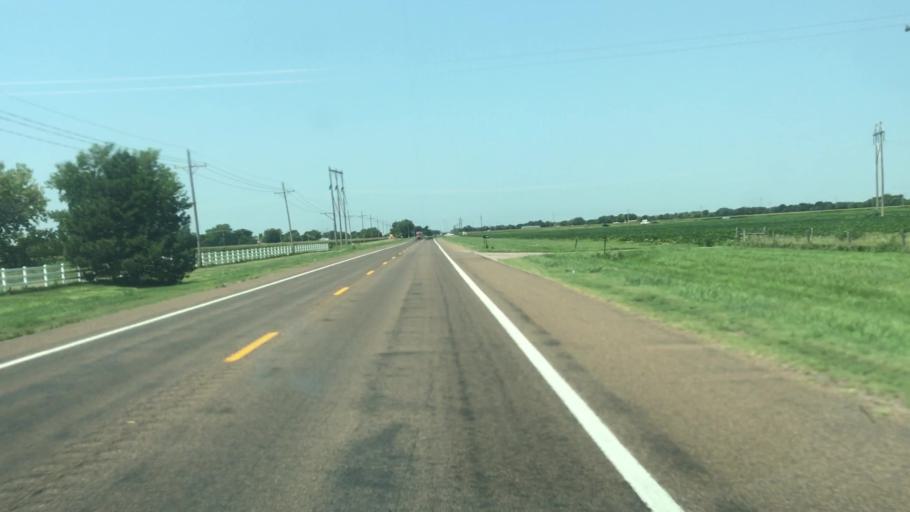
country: US
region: Nebraska
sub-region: Hall County
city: Grand Island
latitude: 40.8869
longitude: -98.3139
